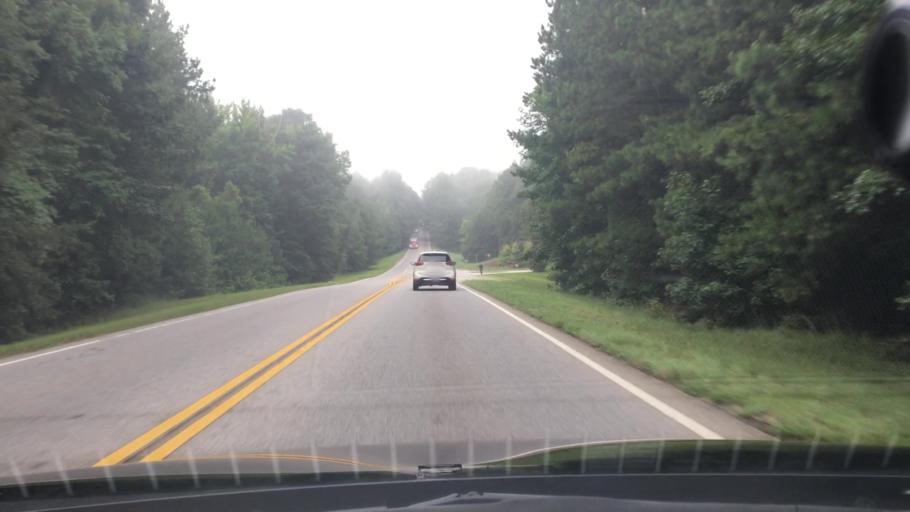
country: US
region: Georgia
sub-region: Coweta County
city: Senoia
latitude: 33.3000
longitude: -84.5388
